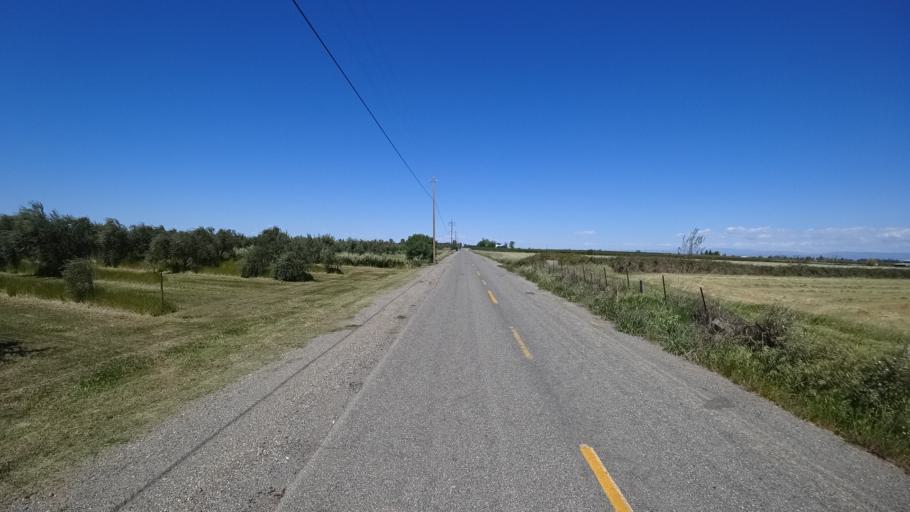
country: US
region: California
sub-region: Glenn County
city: Orland
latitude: 39.7741
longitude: -122.1783
